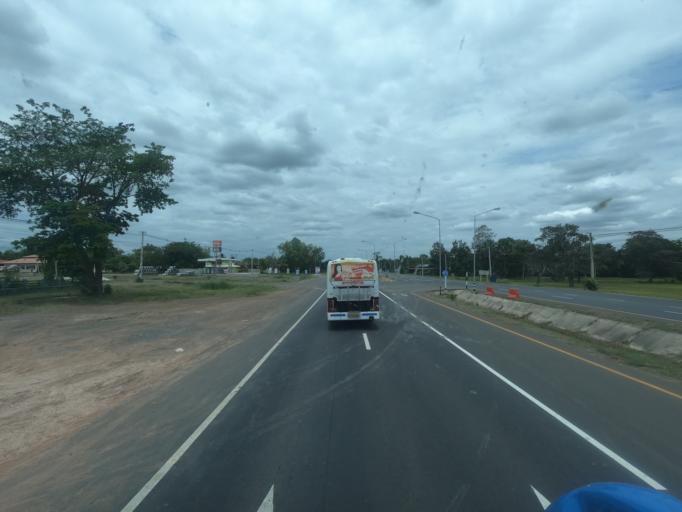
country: TH
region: Buriram
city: Prakhon Chai
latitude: 14.6077
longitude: 103.1302
